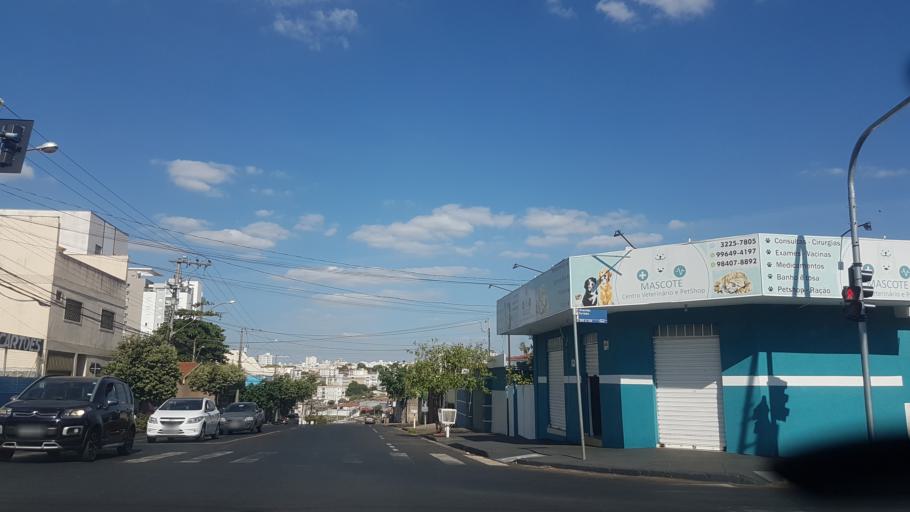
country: BR
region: Minas Gerais
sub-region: Uberlandia
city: Uberlandia
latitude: -18.9073
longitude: -48.2530
